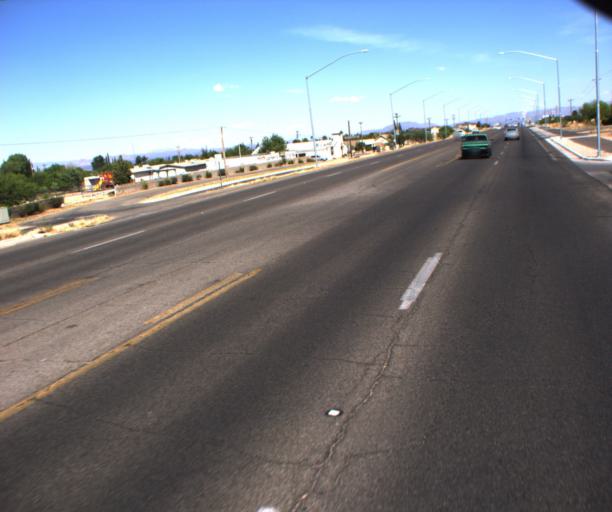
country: US
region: Arizona
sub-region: Cochise County
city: Sierra Vista
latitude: 31.5546
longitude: -110.2512
